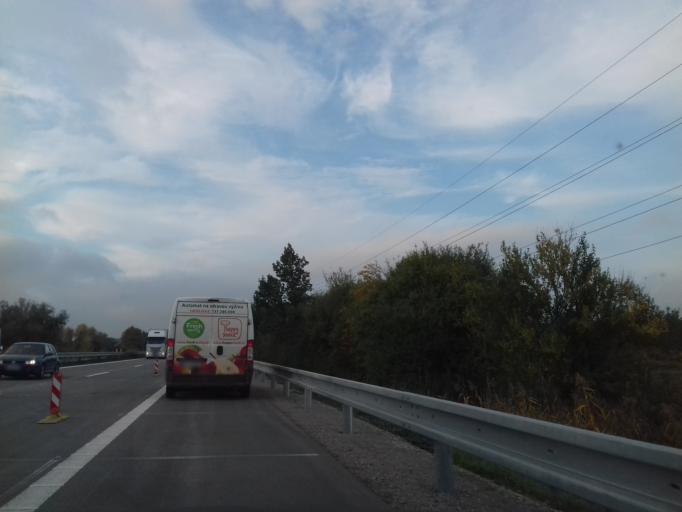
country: CZ
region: South Moravian
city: Nosislav
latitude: 49.0289
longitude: 16.6844
